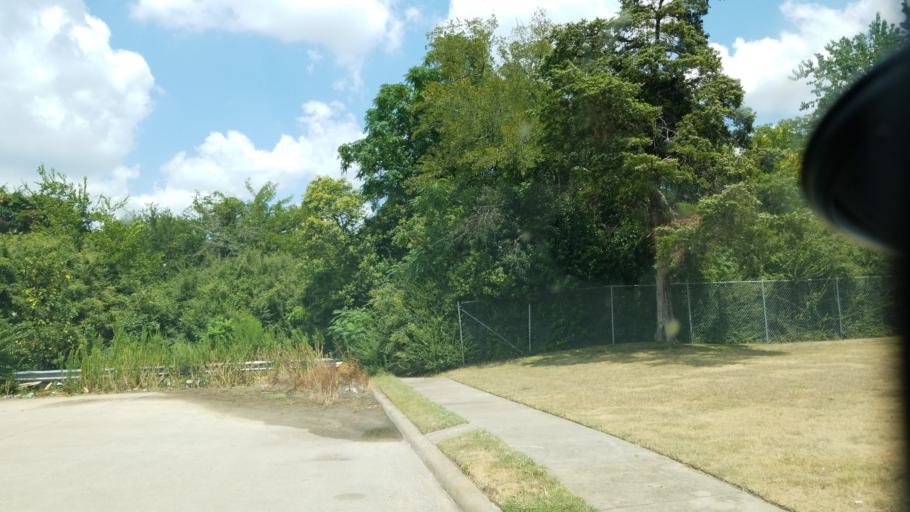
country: US
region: Texas
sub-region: Dallas County
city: Duncanville
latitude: 32.6835
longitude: -96.9039
